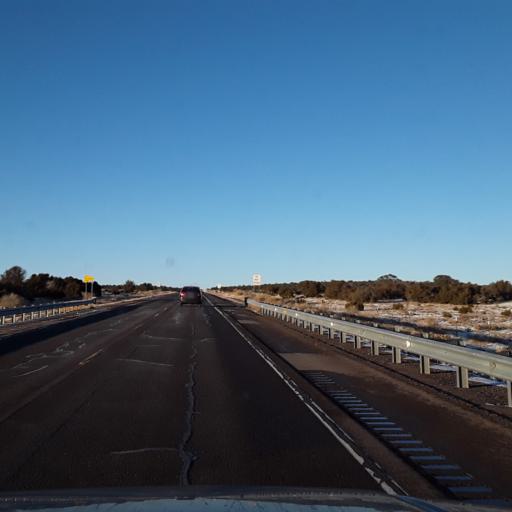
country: US
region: New Mexico
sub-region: Lincoln County
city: Carrizozo
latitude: 34.2068
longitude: -105.6484
